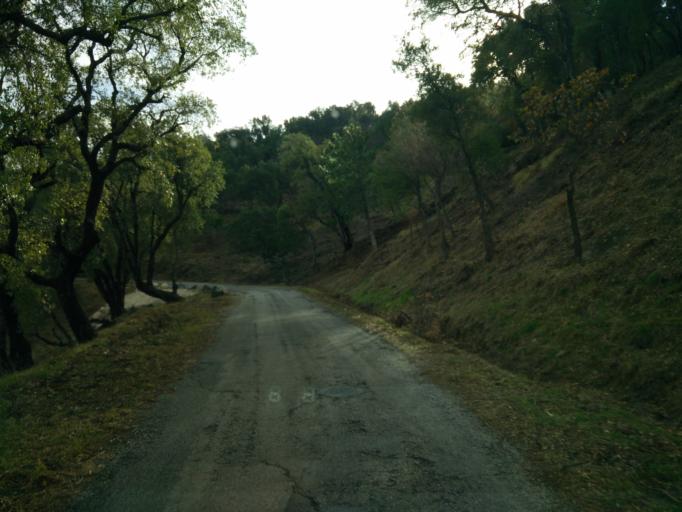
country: FR
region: Provence-Alpes-Cote d'Azur
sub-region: Departement du Var
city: Roquebrune-sur-Argens
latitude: 43.4041
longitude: 6.6291
